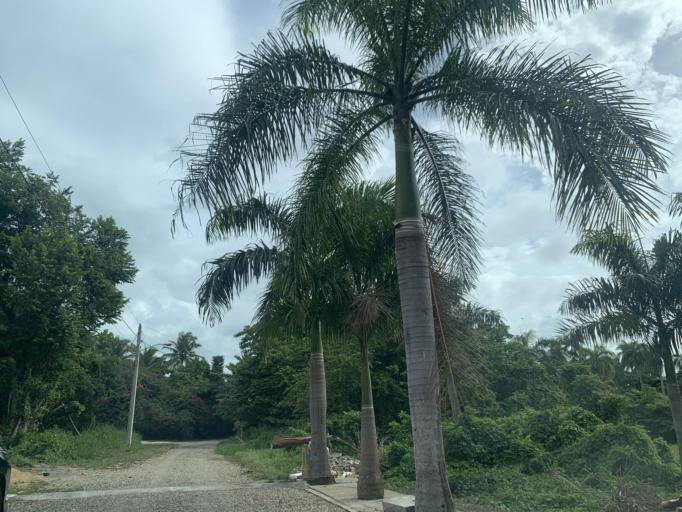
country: DO
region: Puerto Plata
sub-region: Puerto Plata
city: Puerto Plata
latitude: 19.8147
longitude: -70.7206
